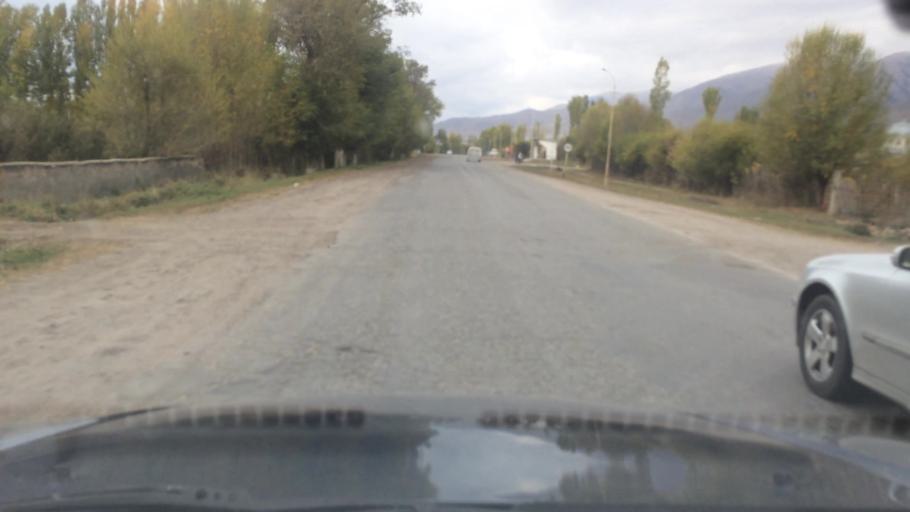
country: KG
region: Ysyk-Koel
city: Tyup
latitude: 42.7851
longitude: 78.2482
